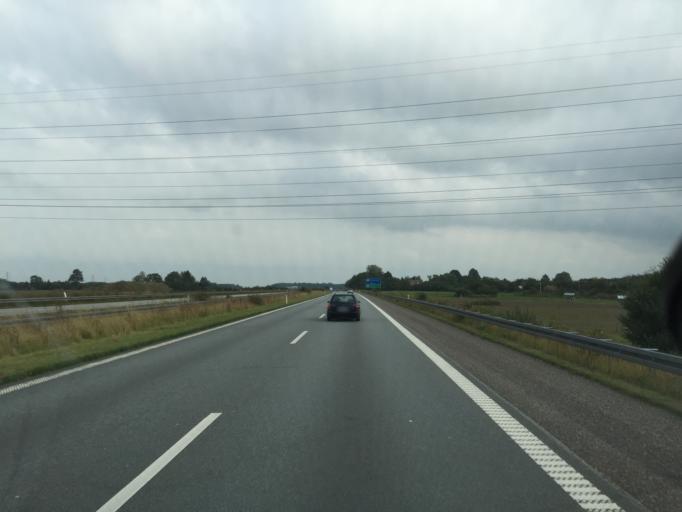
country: DK
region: Zealand
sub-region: Koge Kommune
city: Bjaeverskov
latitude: 55.4649
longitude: 12.0438
